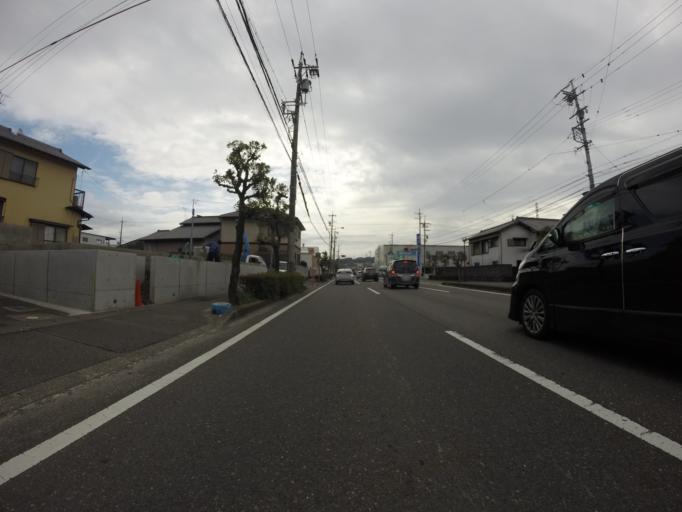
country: JP
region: Shizuoka
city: Shizuoka-shi
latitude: 35.0174
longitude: 138.4443
